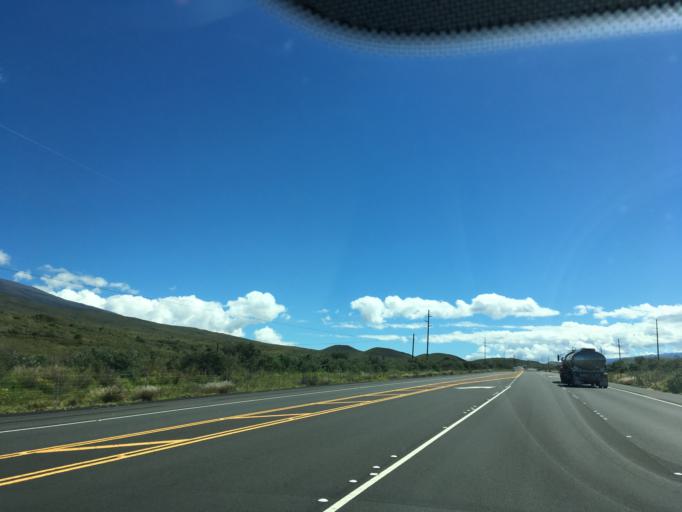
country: US
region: Hawaii
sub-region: Hawaii County
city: Waikoloa
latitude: 19.7900
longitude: -155.6240
